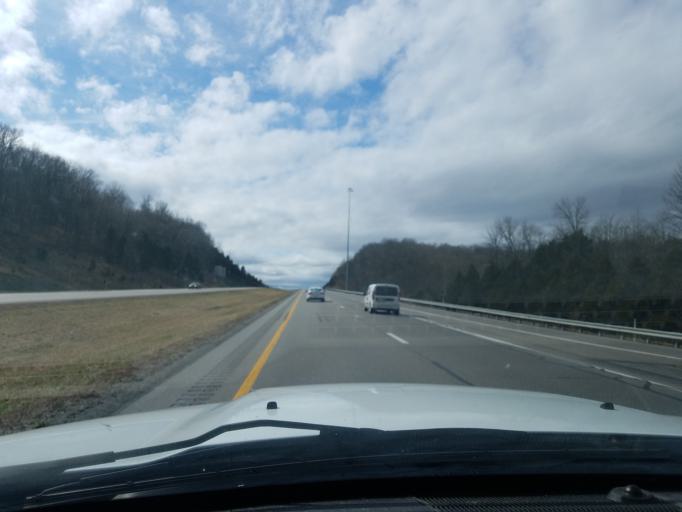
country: US
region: Kentucky
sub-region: Bath County
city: Owingsville
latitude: 38.1260
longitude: -83.7542
